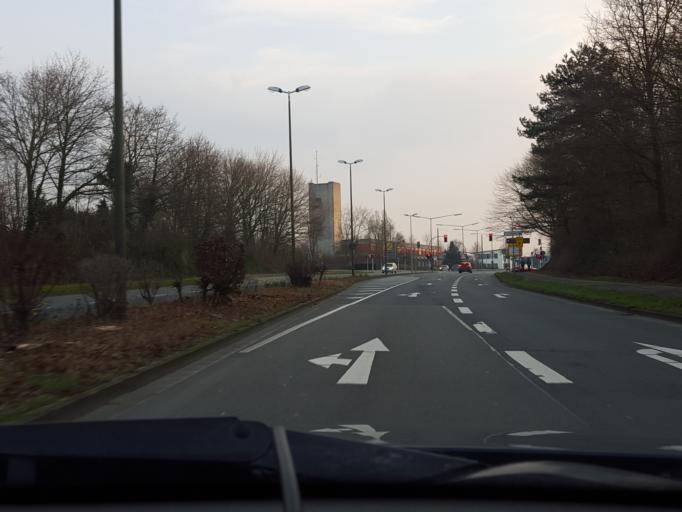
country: DE
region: North Rhine-Westphalia
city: Marl
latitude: 51.6505
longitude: 7.1043
